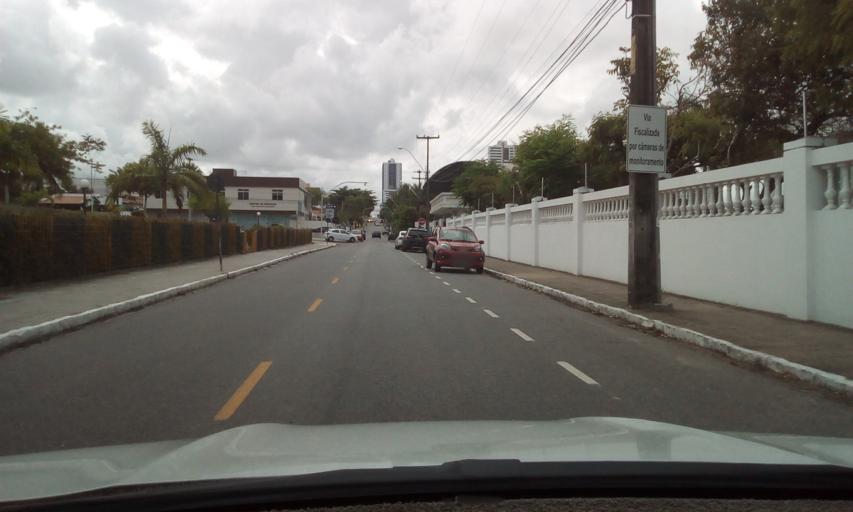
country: BR
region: Paraiba
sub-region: Joao Pessoa
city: Joao Pessoa
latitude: -7.1155
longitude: -34.8448
